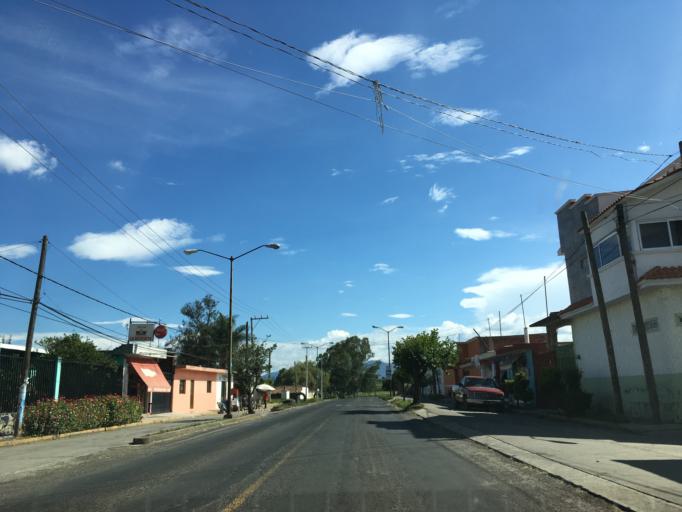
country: MX
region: Michoacan
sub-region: Jimenez
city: Villa Jimenez
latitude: 19.8784
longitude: -101.7733
